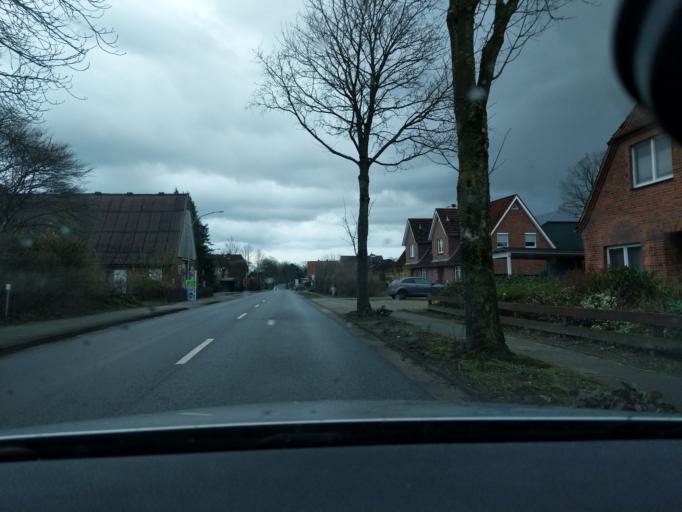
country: DE
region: Lower Saxony
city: Kutenholz
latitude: 53.5091
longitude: 9.3012
